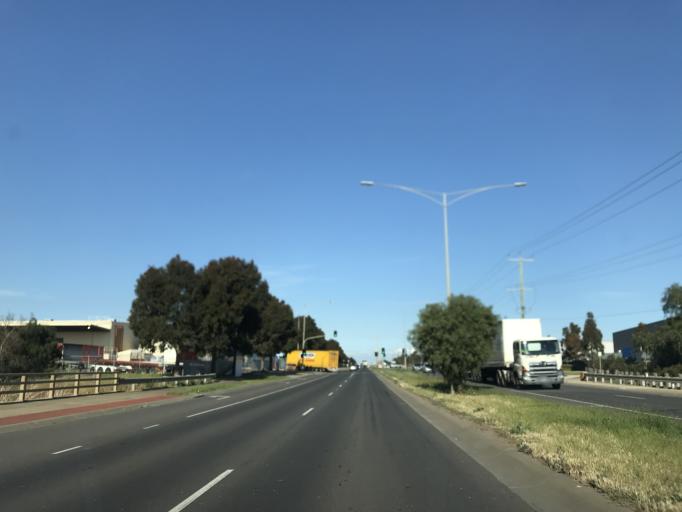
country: AU
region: Victoria
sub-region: Wyndham
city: Truganina
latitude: -37.8112
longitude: 144.7593
